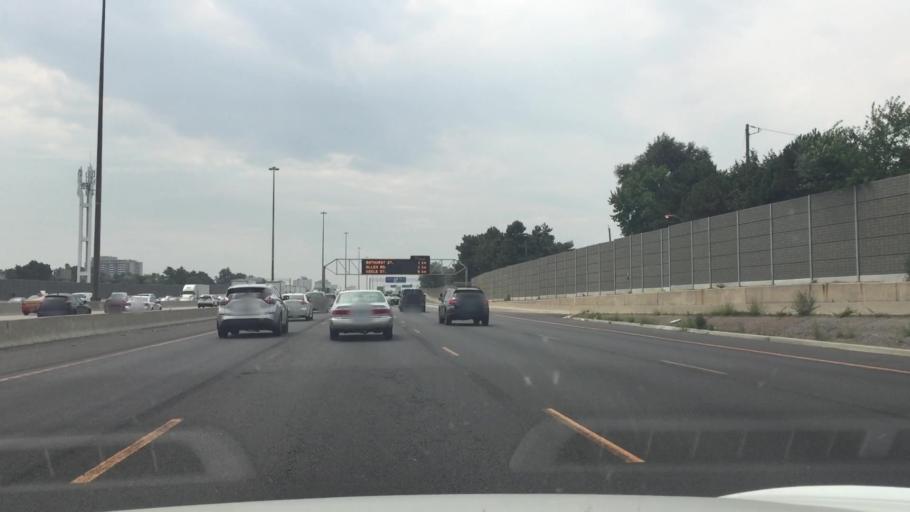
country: CA
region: Ontario
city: North York
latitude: 43.7419
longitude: -79.4254
